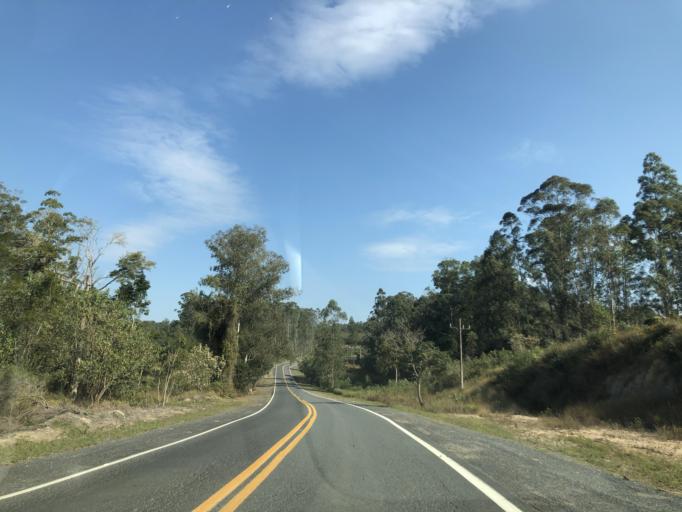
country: BR
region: Sao Paulo
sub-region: Pilar Do Sul
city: Pilar do Sul
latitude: -23.8255
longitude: -47.6644
